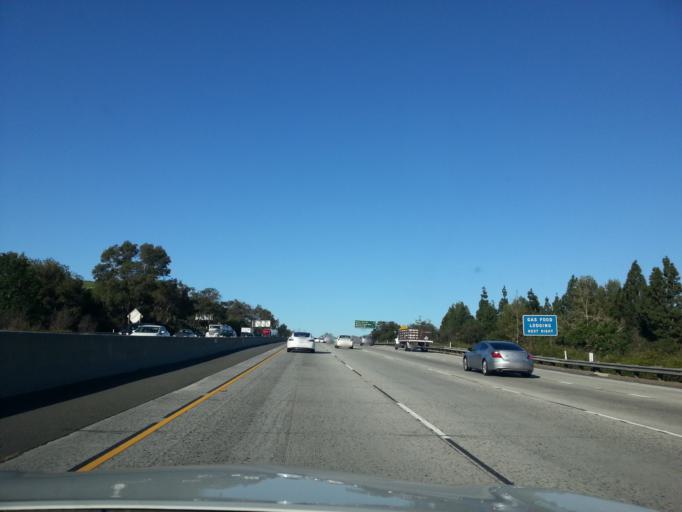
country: US
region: California
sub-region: Ventura County
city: Casa Conejo
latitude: 34.1846
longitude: -118.8987
